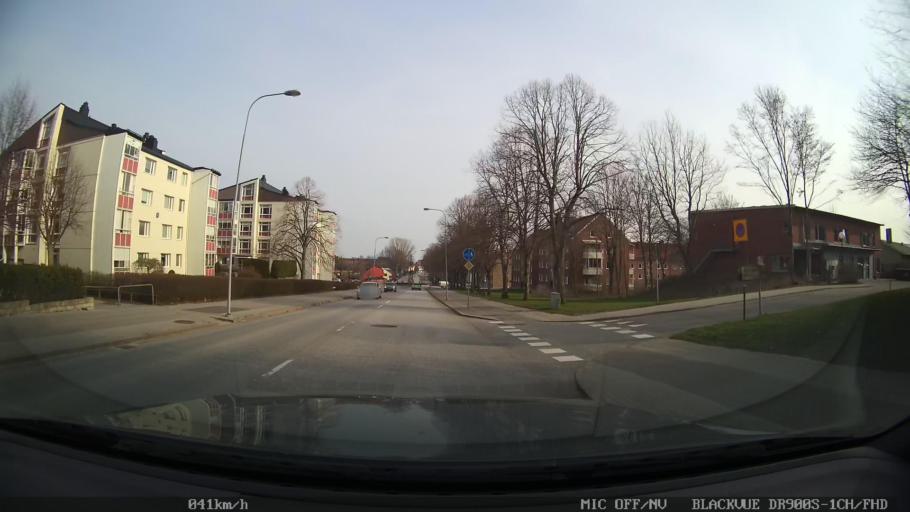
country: SE
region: Skane
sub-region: Ystads Kommun
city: Ystad
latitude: 55.4355
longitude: 13.8120
